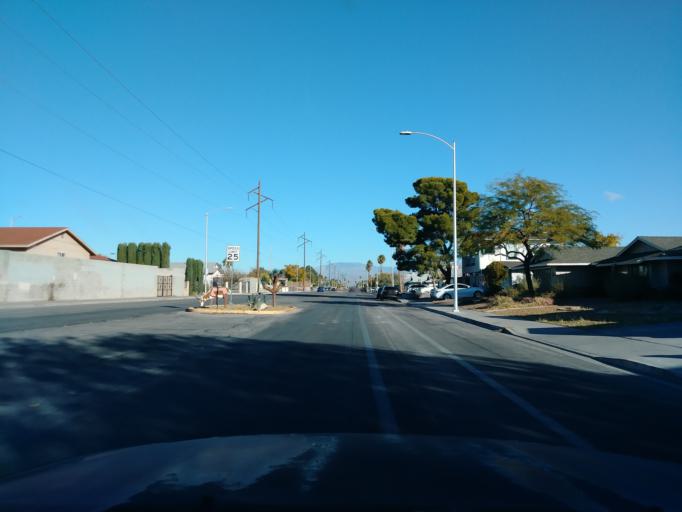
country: US
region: Nevada
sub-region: Clark County
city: Spring Valley
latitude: 36.1632
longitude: -115.2508
